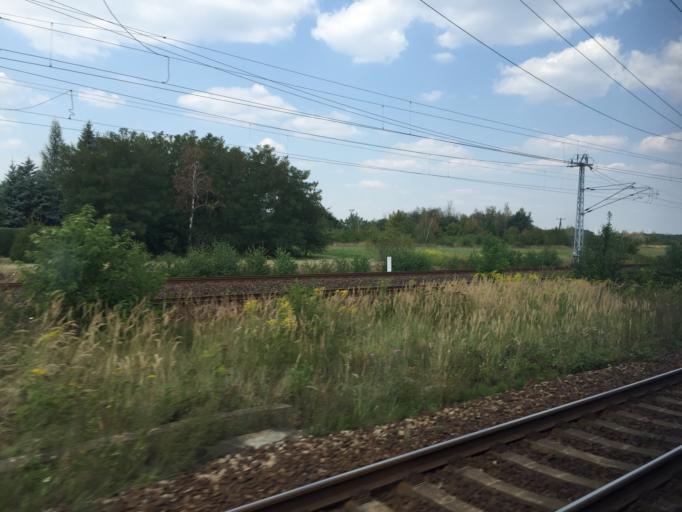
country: DE
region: Brandenburg
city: Grossraschen
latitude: 51.5550
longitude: 14.0569
